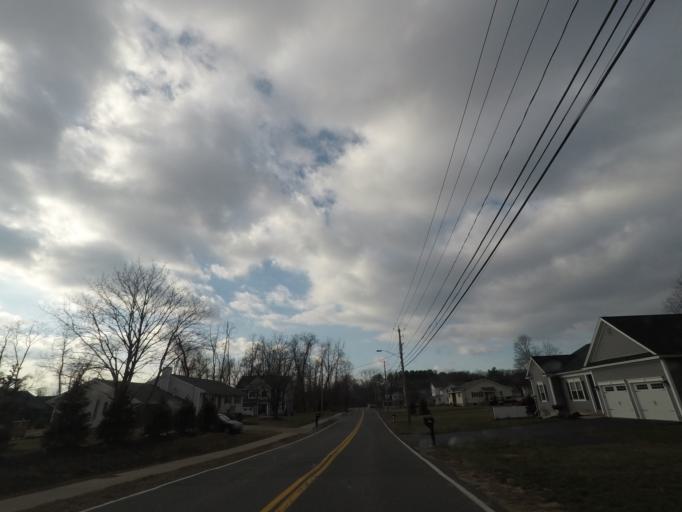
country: US
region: New York
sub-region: Albany County
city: McKownville
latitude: 42.6651
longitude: -73.8360
